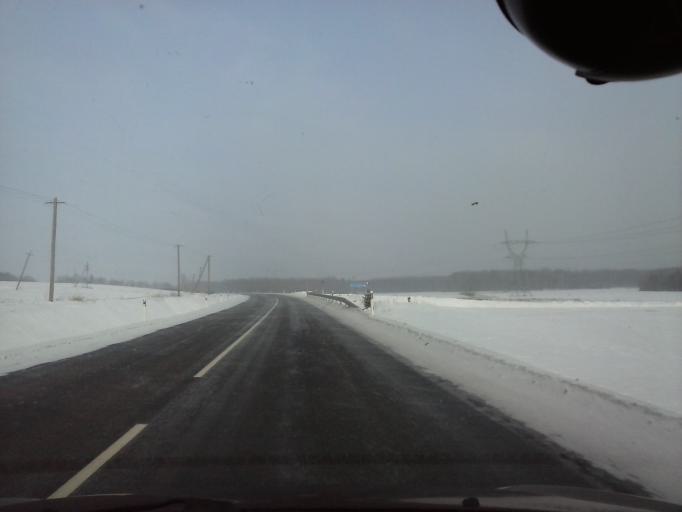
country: EE
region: Viljandimaa
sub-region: Abja vald
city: Abja-Paluoja
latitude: 58.2826
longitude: 25.2866
